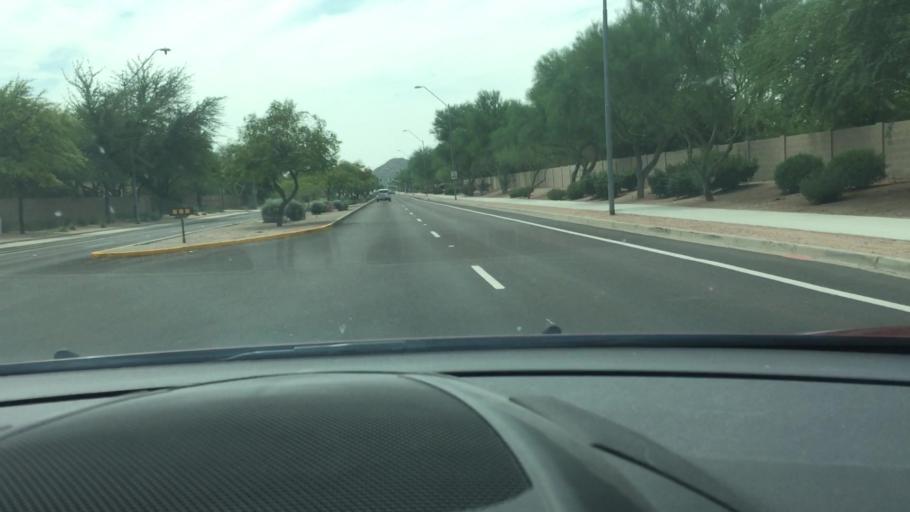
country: US
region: Arizona
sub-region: Maricopa County
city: Scottsdale
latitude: 33.5385
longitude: -111.9002
